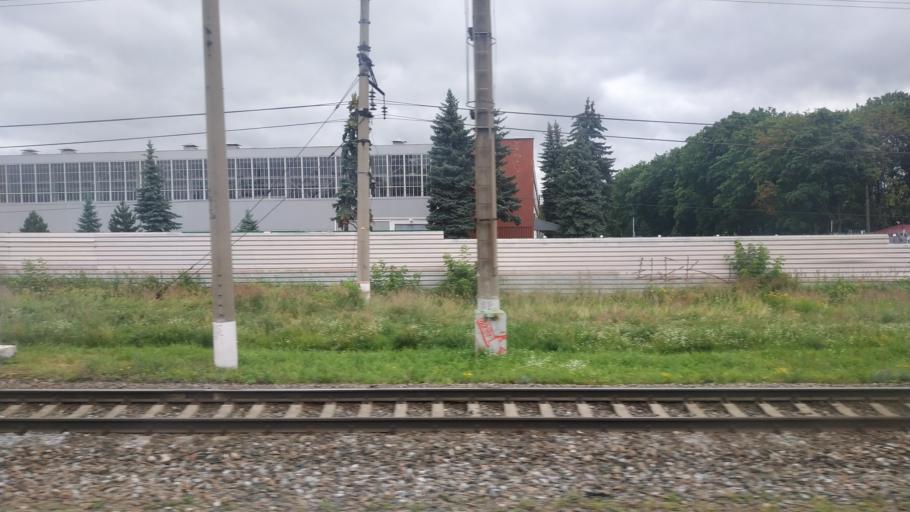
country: RU
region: Moskovskaya
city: Tomilino
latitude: 55.6623
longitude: 37.9370
